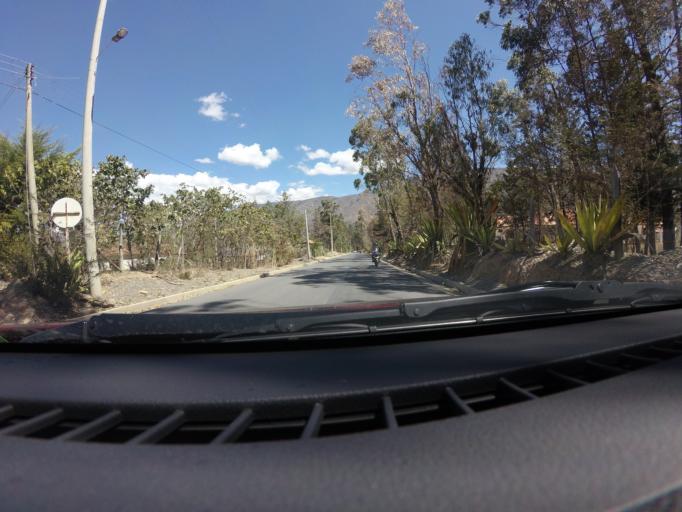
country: CO
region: Boyaca
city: Villa de Leiva
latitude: 5.6286
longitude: -73.5396
